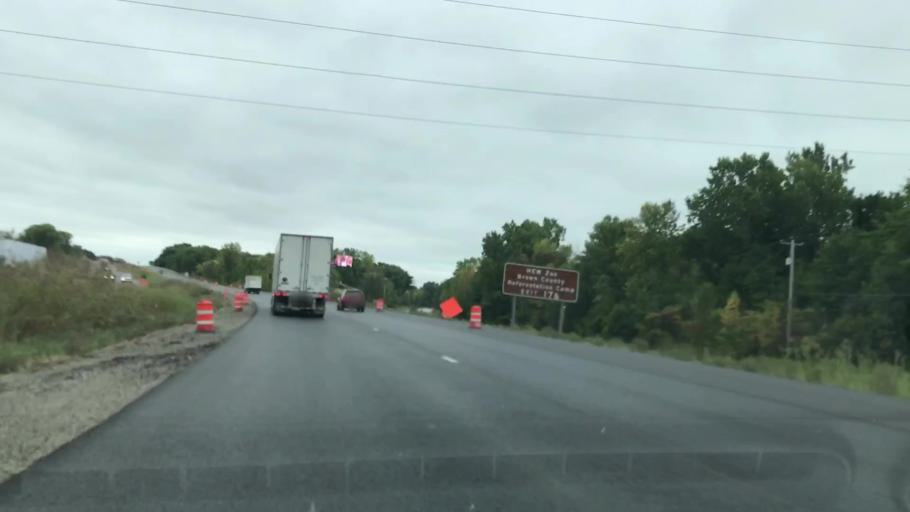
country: US
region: Wisconsin
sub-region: Brown County
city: Suamico
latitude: 44.6464
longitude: -88.0499
